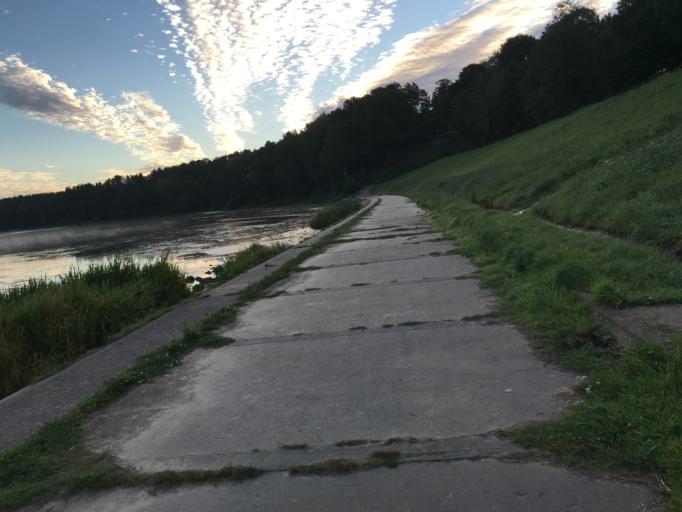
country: LT
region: Alytaus apskritis
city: Druskininkai
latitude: 54.0189
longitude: 23.9847
